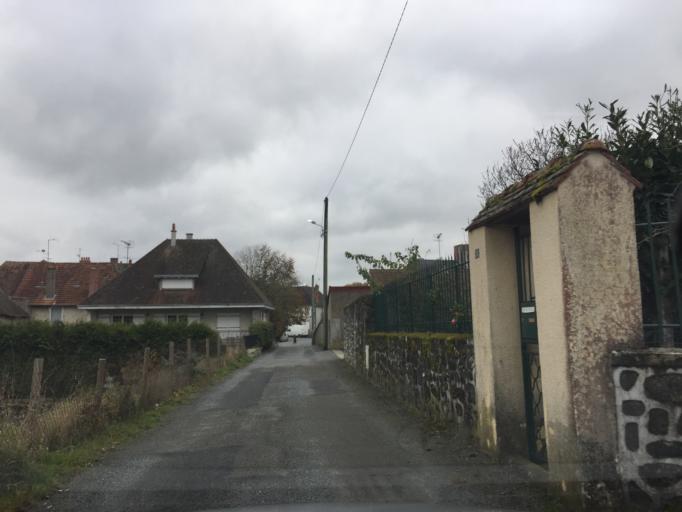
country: FR
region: Limousin
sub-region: Departement de la Creuse
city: Ahun
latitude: 46.0858
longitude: 2.0438
